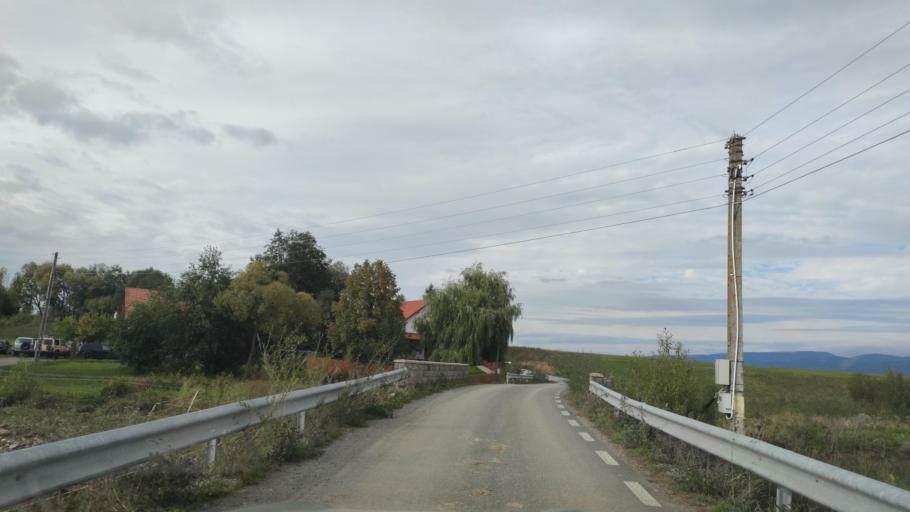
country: RO
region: Harghita
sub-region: Comuna Remetea
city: Remetea
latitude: 46.8127
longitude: 25.4225
